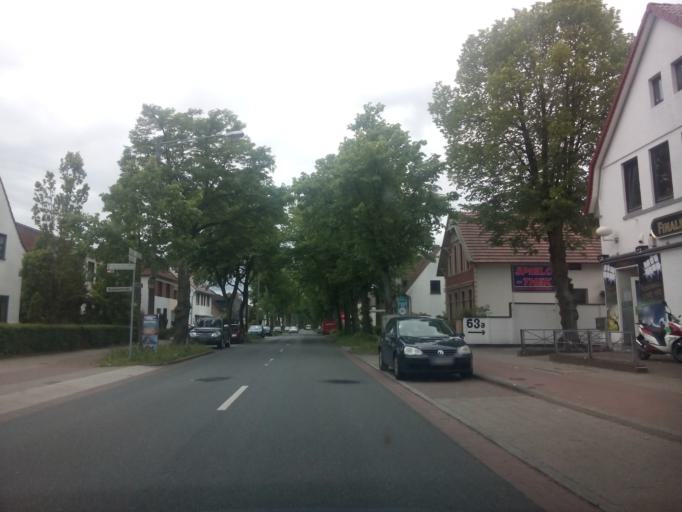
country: DE
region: Lower Saxony
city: Schwanewede
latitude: 53.2008
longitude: 8.5742
